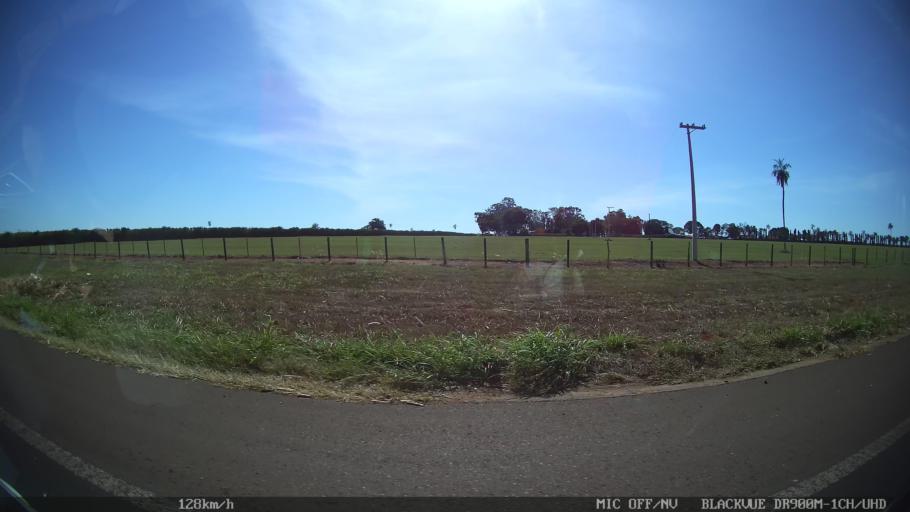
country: BR
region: Sao Paulo
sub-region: Barretos
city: Barretos
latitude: -20.5694
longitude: -48.6686
